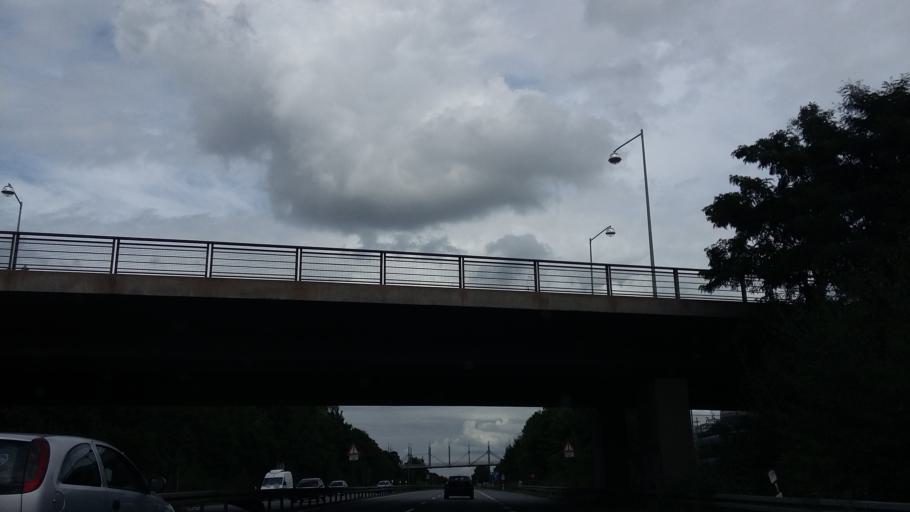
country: DE
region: Lower Saxony
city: Laatzen
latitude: 52.3186
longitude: 9.8135
